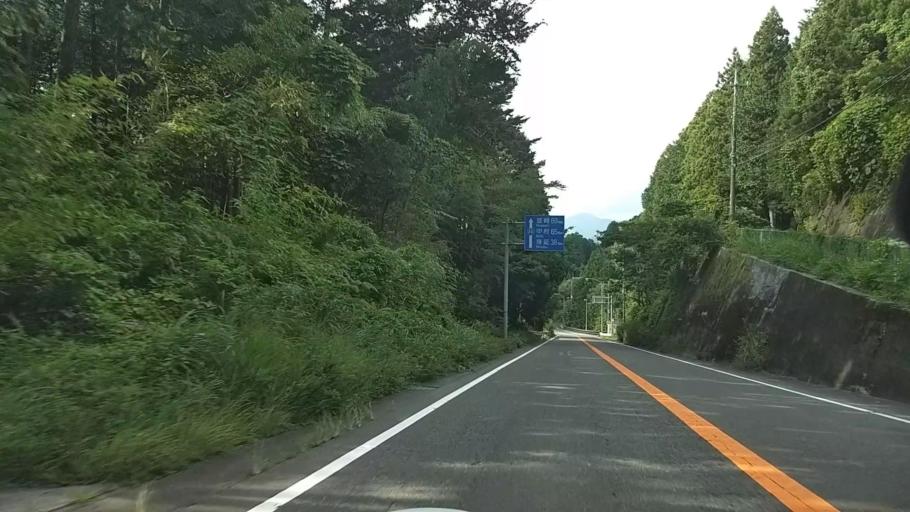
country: JP
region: Shizuoka
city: Fujinomiya
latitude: 35.2124
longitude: 138.5193
